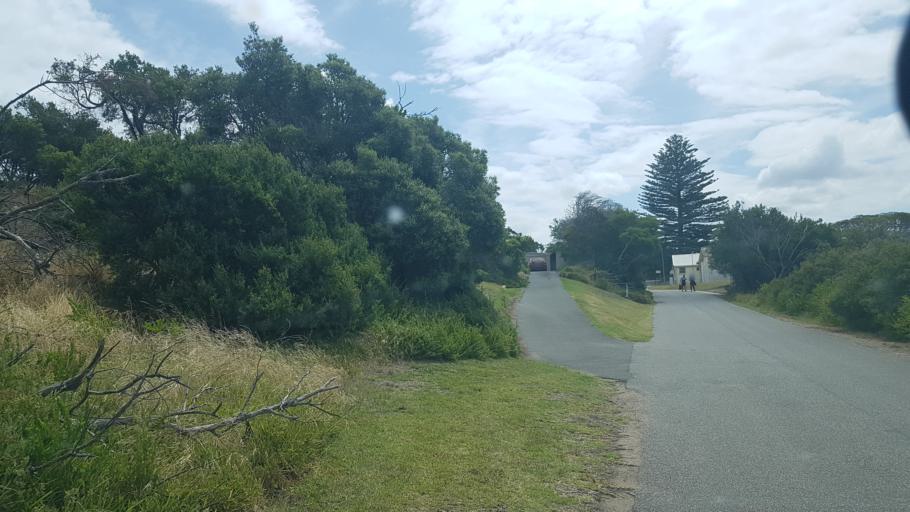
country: AU
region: Victoria
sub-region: Mornington Peninsula
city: Sorrento
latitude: -38.3155
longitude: 144.7014
